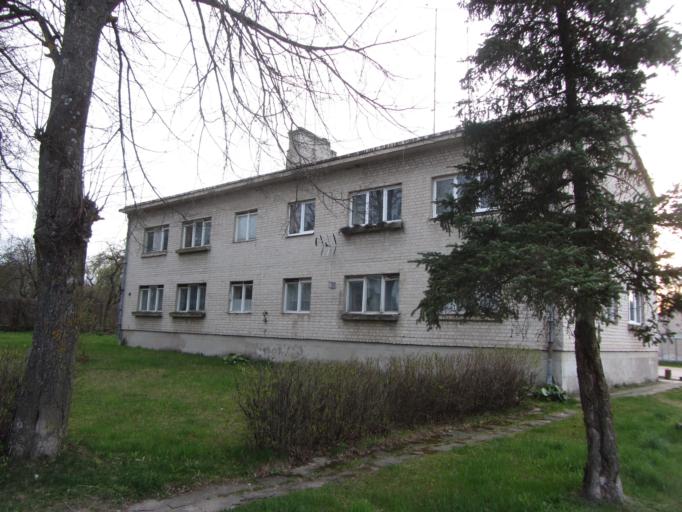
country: LT
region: Utenos apskritis
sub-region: Utena
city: Utena
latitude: 55.7371
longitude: 25.8331
